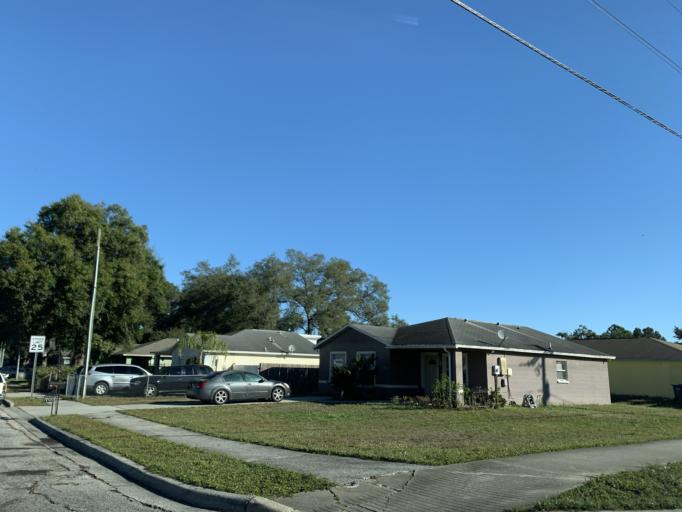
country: US
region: Florida
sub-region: Hillsborough County
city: Temple Terrace
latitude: 28.0290
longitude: -82.4275
